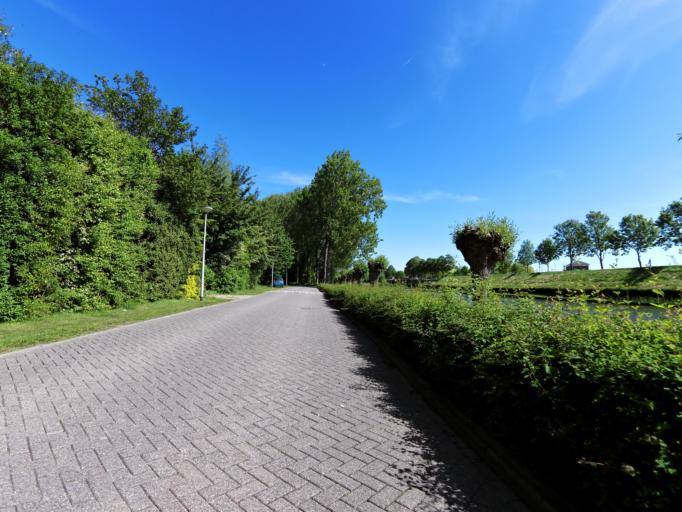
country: NL
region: South Holland
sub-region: Gemeente Hellevoetsluis
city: Hellevoetsluis
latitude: 51.8304
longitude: 4.1284
